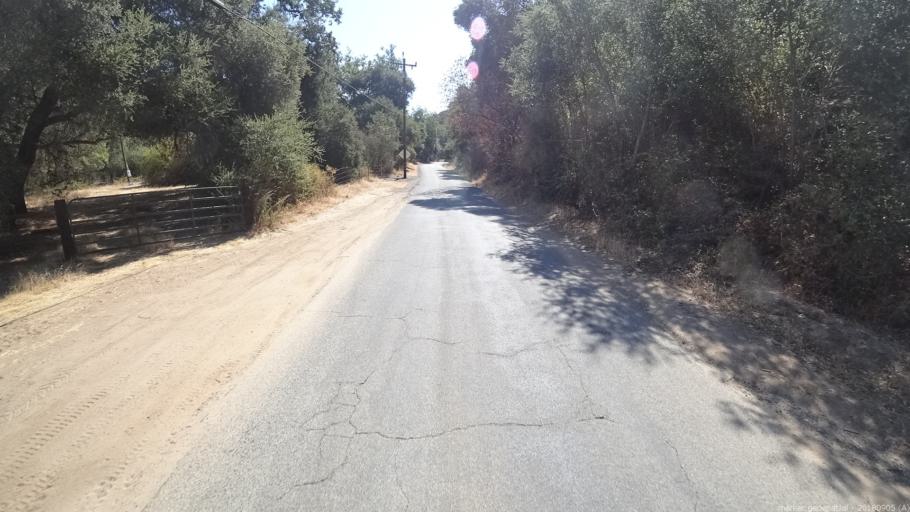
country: US
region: California
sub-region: Monterey County
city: Carmel Valley Village
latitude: 36.3920
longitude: -121.6252
